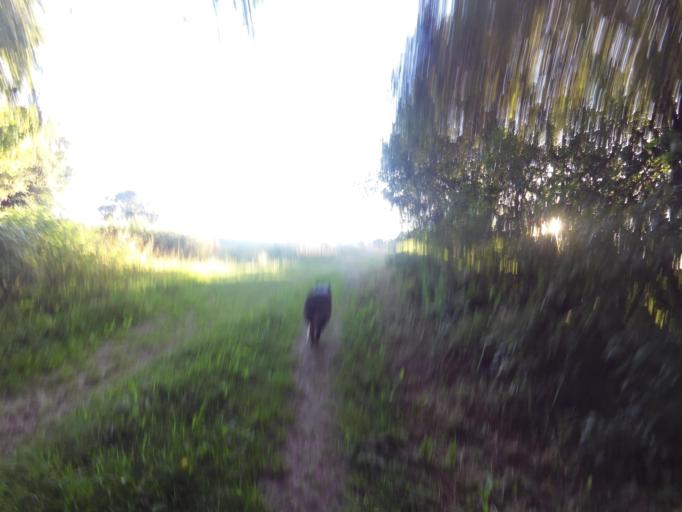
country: FR
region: Brittany
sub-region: Departement du Morbihan
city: Molac
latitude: 47.7228
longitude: -2.4330
